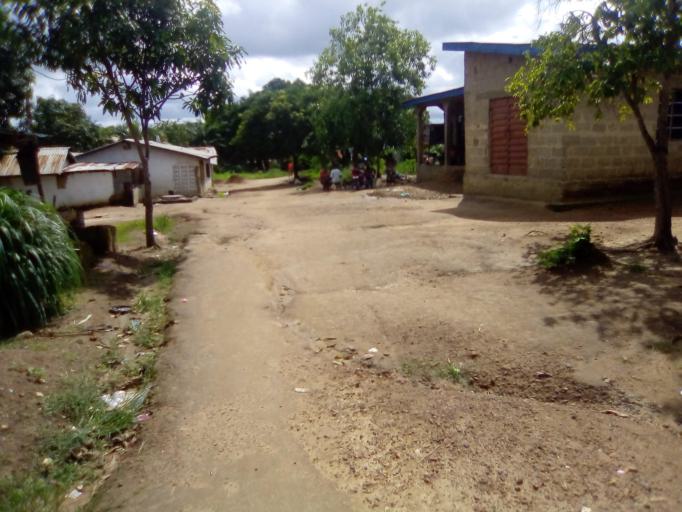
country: SL
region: Southern Province
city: Baoma
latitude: 7.9850
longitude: -11.7230
